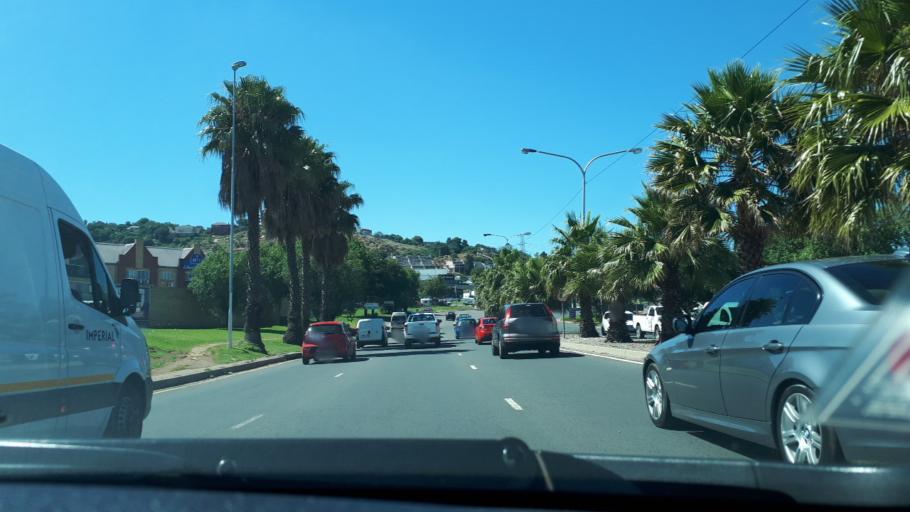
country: ZA
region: Gauteng
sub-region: Ekurhuleni Metropolitan Municipality
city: Germiston
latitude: -26.1645
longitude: 28.1675
